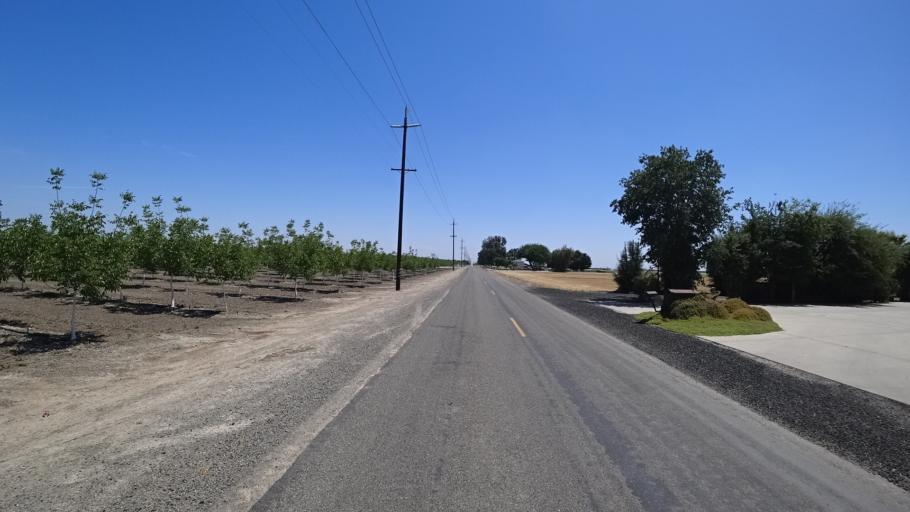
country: US
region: California
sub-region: Kings County
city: Armona
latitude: 36.2402
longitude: -119.7201
